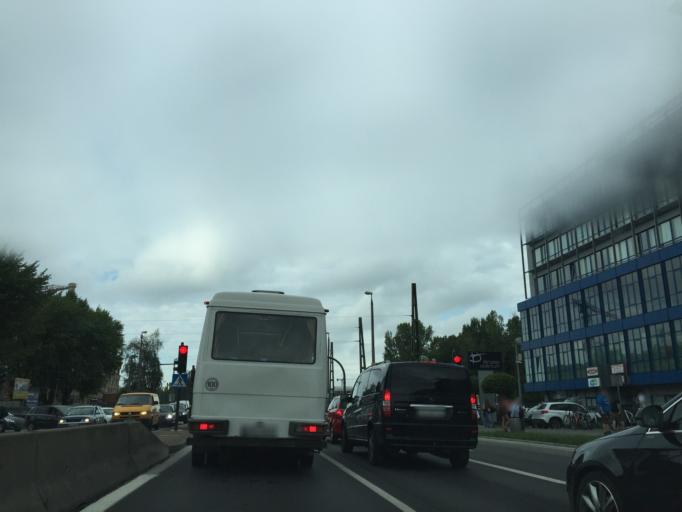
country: PL
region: Lesser Poland Voivodeship
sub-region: Krakow
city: Krakow
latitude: 50.0327
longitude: 19.9385
